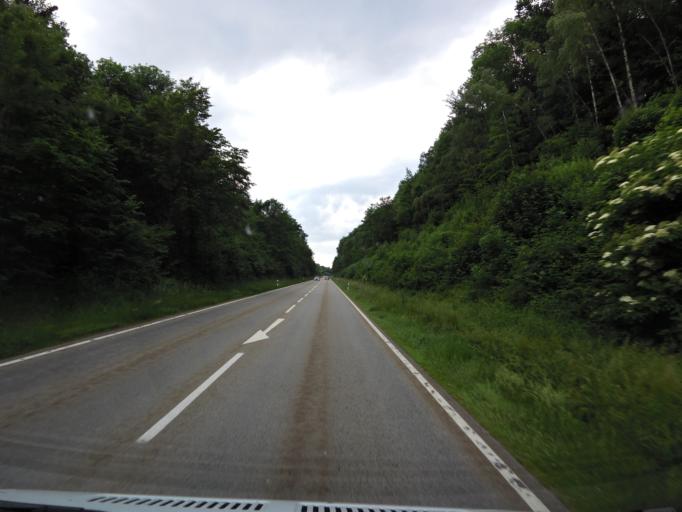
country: DE
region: Bavaria
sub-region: Lower Bavaria
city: Witzmannsberg
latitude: 48.6896
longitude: 13.4166
